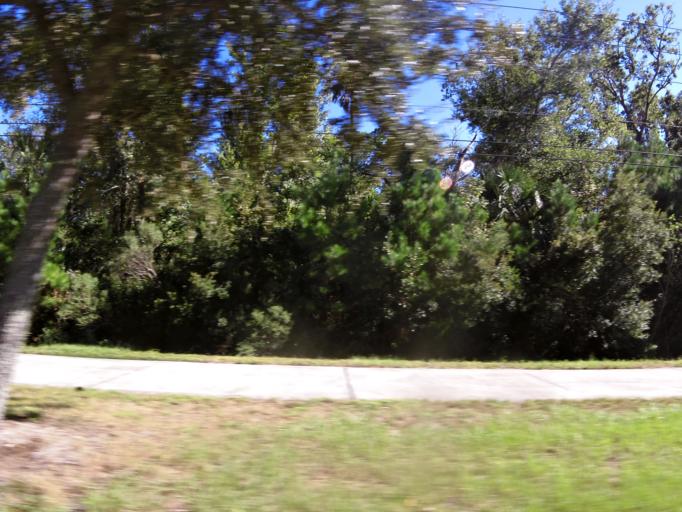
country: US
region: Florida
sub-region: Saint Johns County
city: Palm Valley
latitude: 30.1263
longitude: -81.3947
